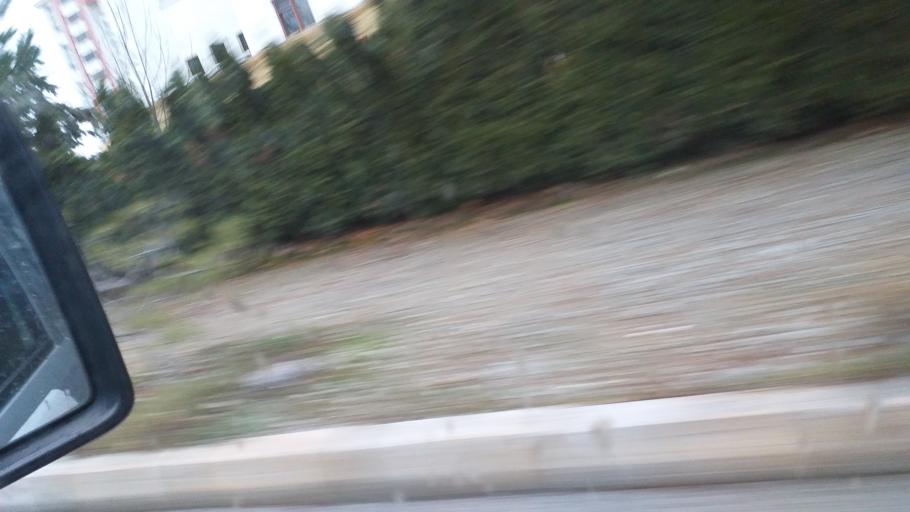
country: TR
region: Ankara
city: Batikent
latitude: 39.8770
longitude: 32.7166
